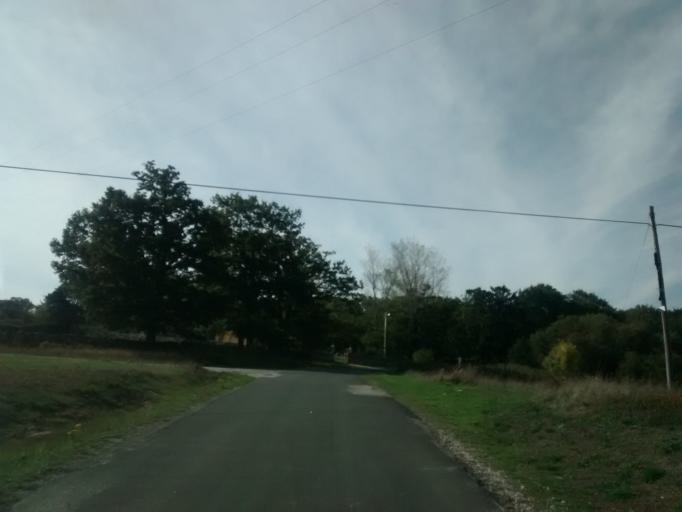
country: ES
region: Castille and Leon
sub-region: Provincia de Burgos
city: Arija
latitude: 42.9654
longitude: -3.9583
